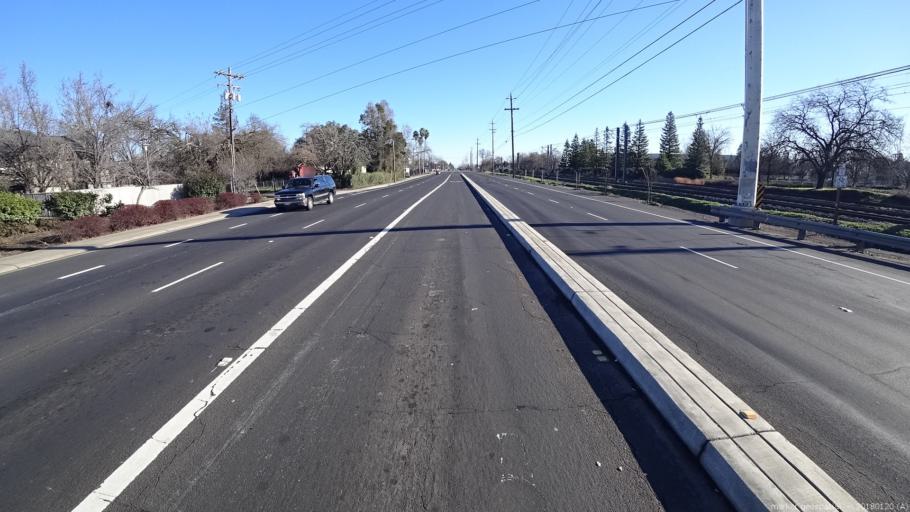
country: US
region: California
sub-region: Sacramento County
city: La Riviera
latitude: 38.5685
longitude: -121.3444
